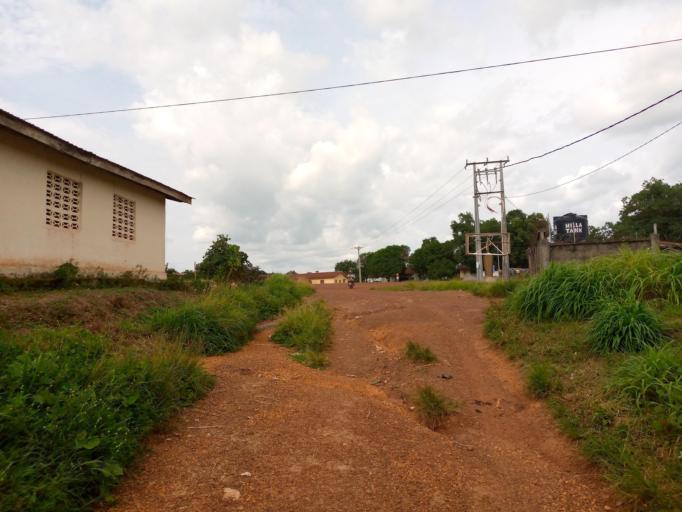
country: SL
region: Northern Province
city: Magburaka
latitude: 8.7218
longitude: -11.9412
